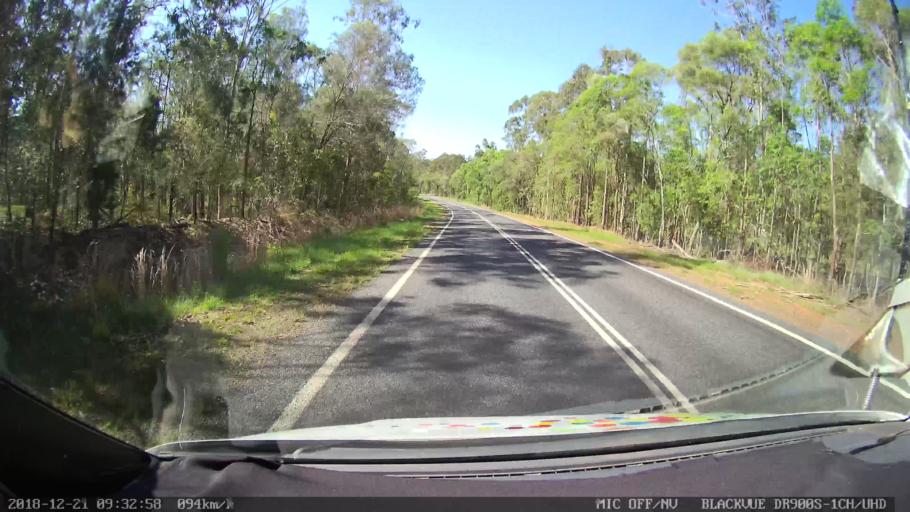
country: AU
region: New South Wales
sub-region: Clarence Valley
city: Grafton
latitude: -29.4776
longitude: 152.9763
